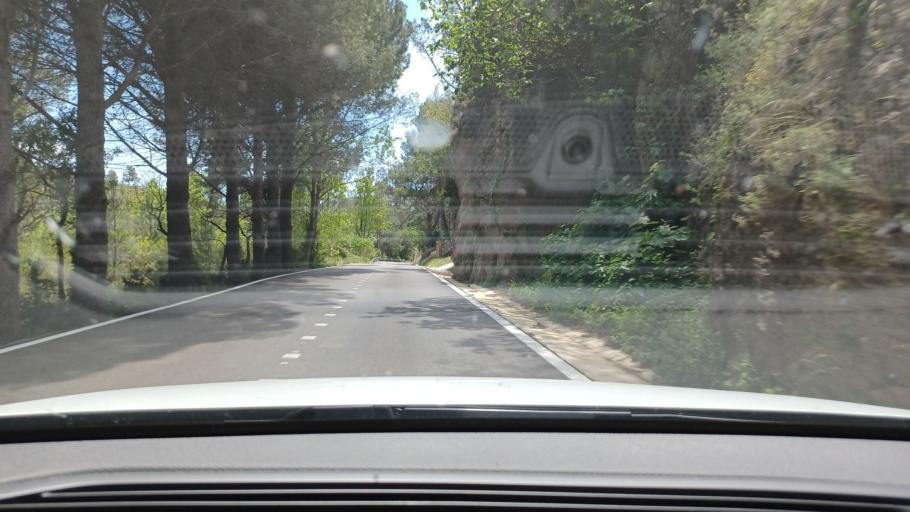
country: ES
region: Valencia
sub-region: Provincia de Castello
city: Rosell
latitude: 40.6655
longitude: 0.2646
